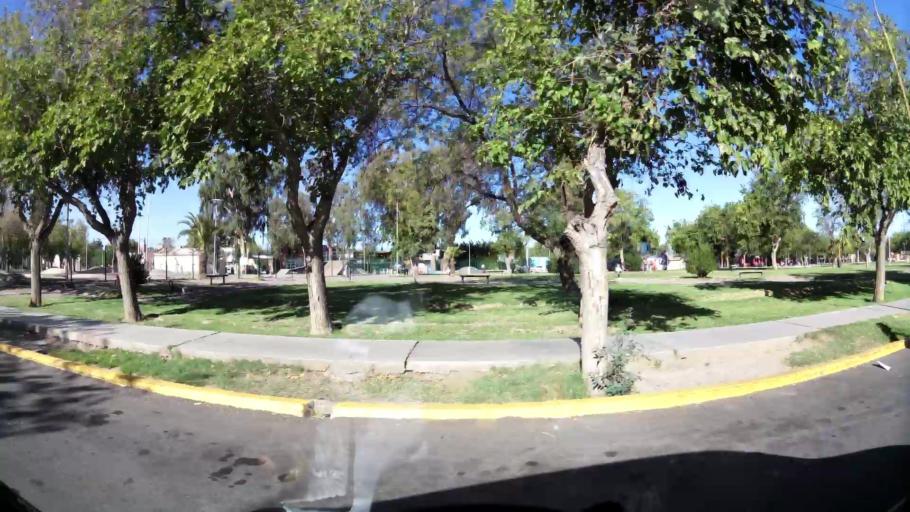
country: AR
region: San Juan
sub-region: Departamento de Santa Lucia
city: Santa Lucia
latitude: -31.5377
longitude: -68.5098
